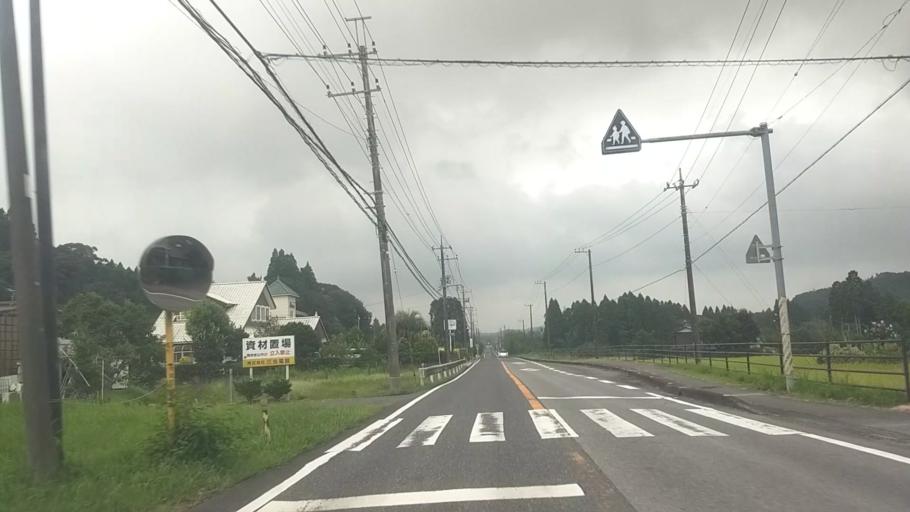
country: JP
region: Chiba
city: Ohara
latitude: 35.2845
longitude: 140.2713
